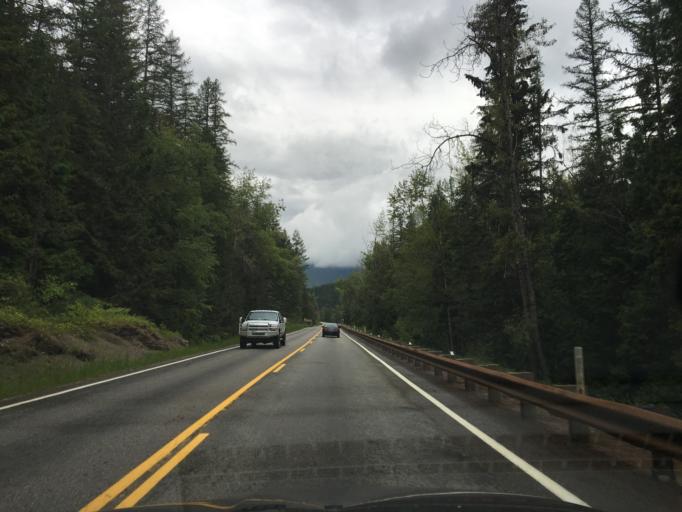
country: US
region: Montana
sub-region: Flathead County
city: Columbia Falls
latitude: 48.4957
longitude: -113.9601
